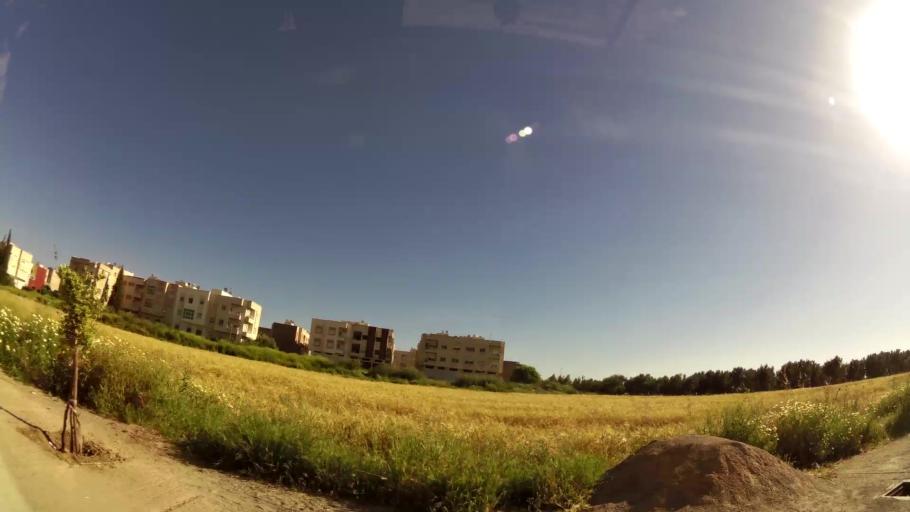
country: MA
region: Fes-Boulemane
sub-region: Fes
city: Fes
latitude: 34.0103
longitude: -5.0176
